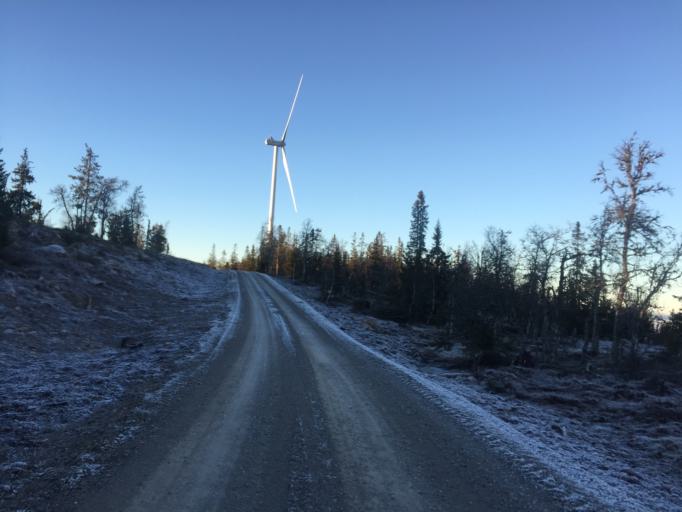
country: NO
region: Hedmark
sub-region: Elverum
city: Elverum
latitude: 61.2110
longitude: 11.7848
